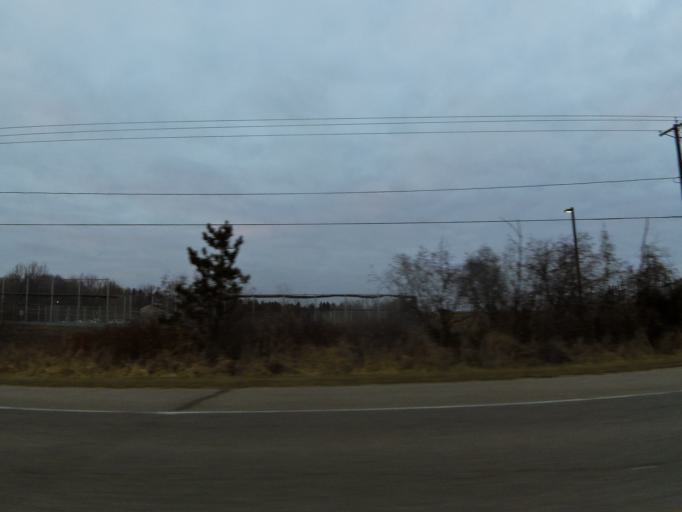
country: US
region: Minnesota
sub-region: Washington County
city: Mahtomedi
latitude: 45.0575
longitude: -92.9385
